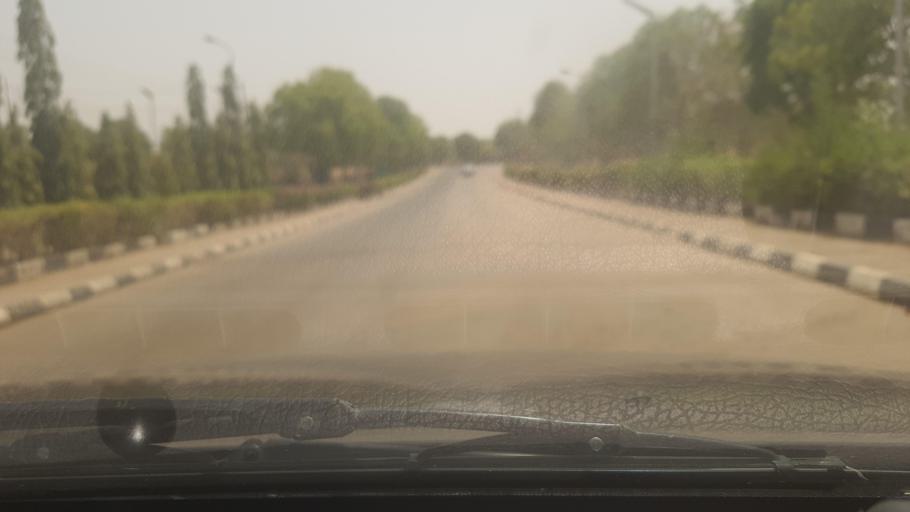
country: NG
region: Gombe
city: Gombe
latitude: 10.3047
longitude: 11.1739
